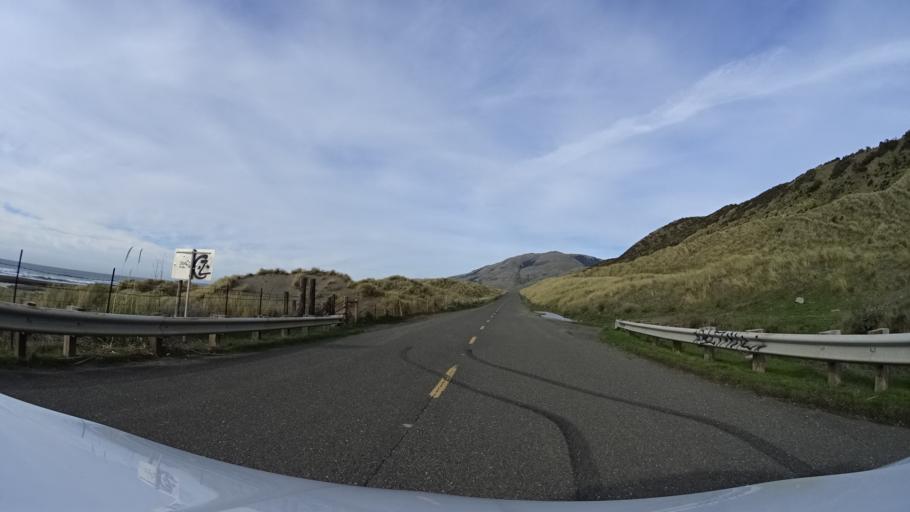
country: US
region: California
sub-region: Humboldt County
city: Ferndale
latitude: 40.3529
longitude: -124.3610
